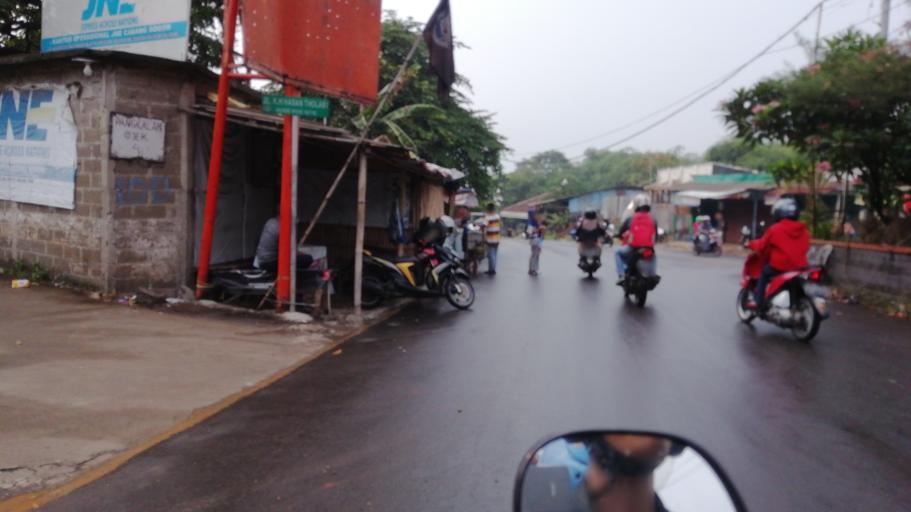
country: ID
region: West Java
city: Bogor
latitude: -6.5341
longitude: 106.8067
